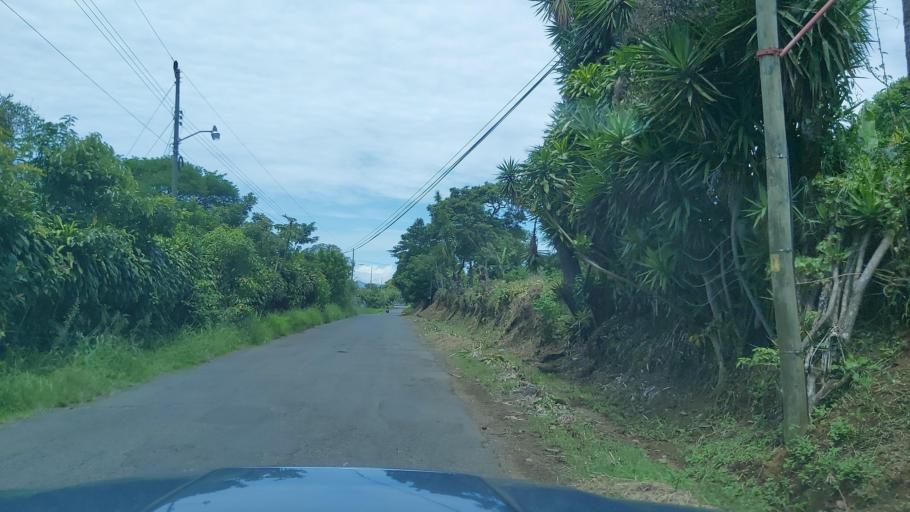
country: CR
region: Alajuela
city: San Juan
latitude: 10.1019
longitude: -84.3351
